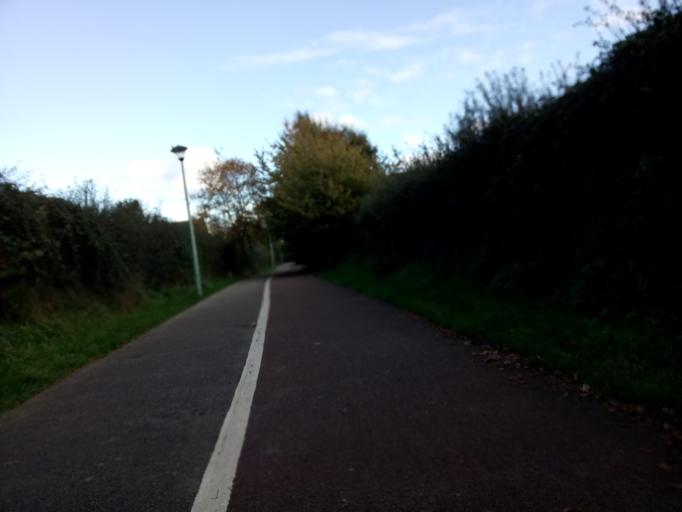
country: GB
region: England
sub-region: Suffolk
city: Kesgrave
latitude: 52.0621
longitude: 1.2460
